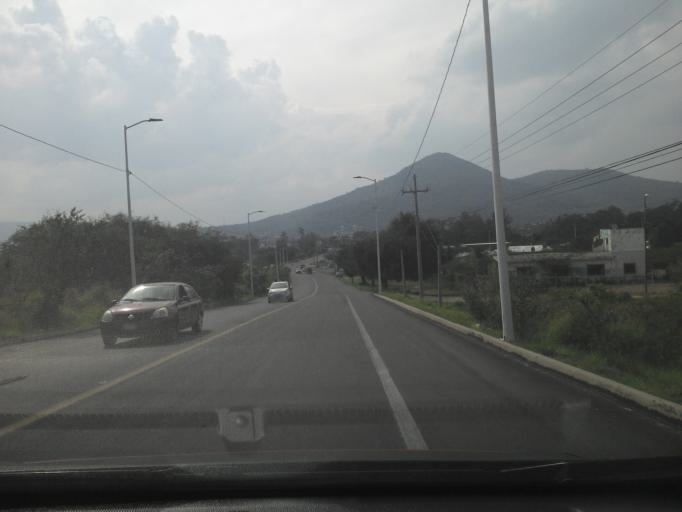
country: MX
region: Jalisco
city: Tlajomulco de Zuniga
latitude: 20.4784
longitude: -103.4366
